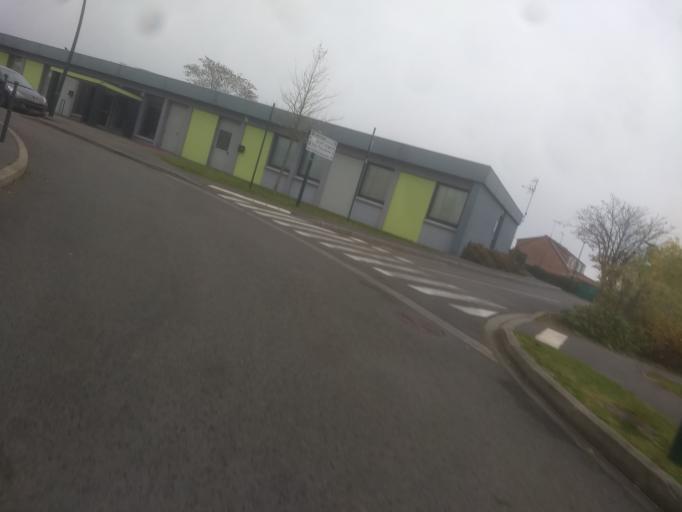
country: FR
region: Nord-Pas-de-Calais
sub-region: Departement du Pas-de-Calais
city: Saint-Laurent-Blangy
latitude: 50.3025
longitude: 2.7949
